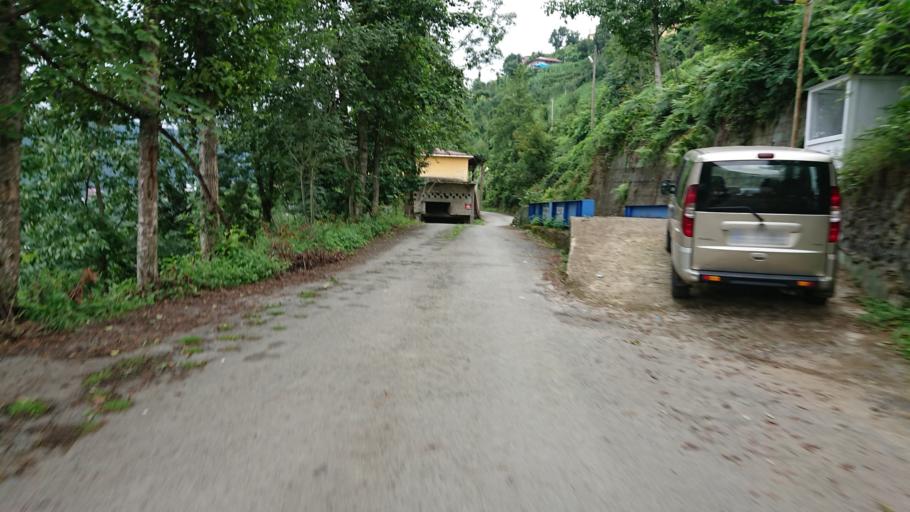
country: TR
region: Rize
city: Rize
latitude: 40.9708
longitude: 40.5166
